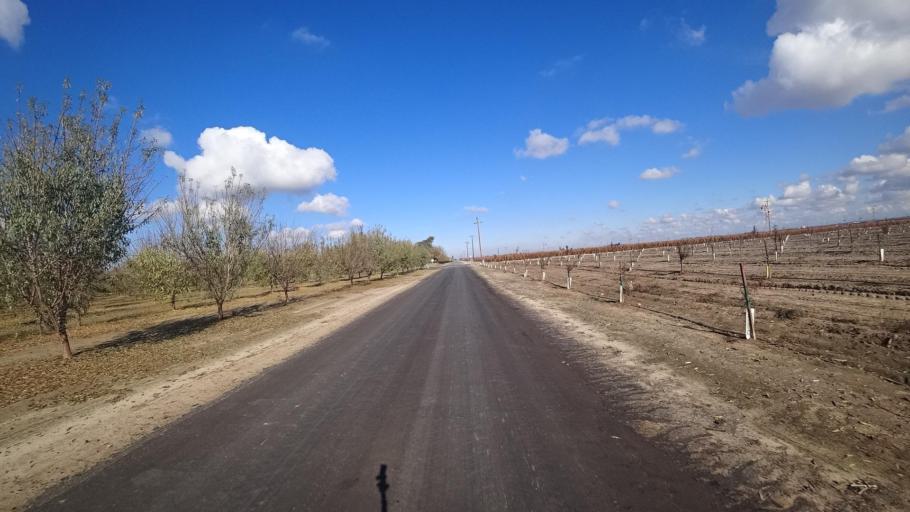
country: US
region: California
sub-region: Kern County
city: McFarland
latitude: 35.6444
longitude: -119.2322
